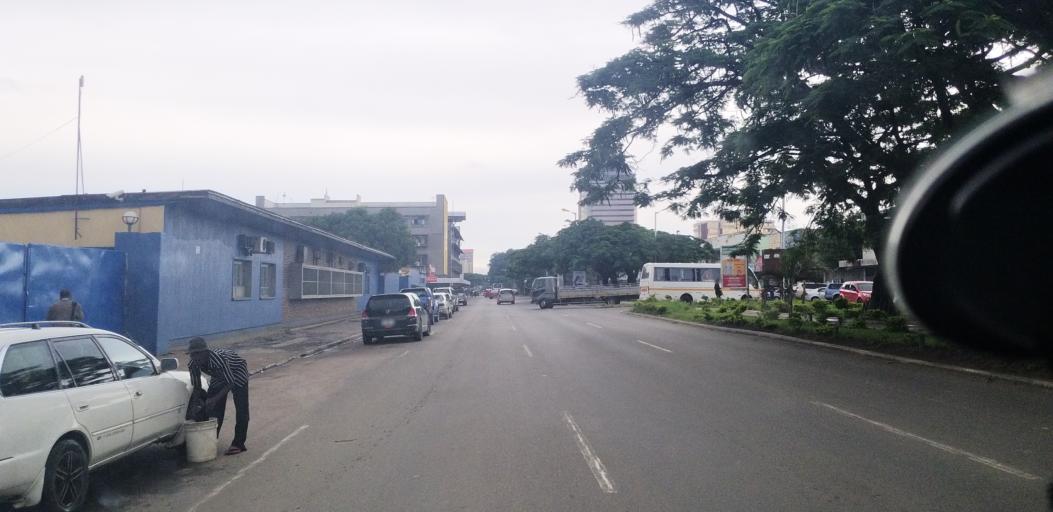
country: ZM
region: Lusaka
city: Lusaka
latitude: -15.4135
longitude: 28.2813
